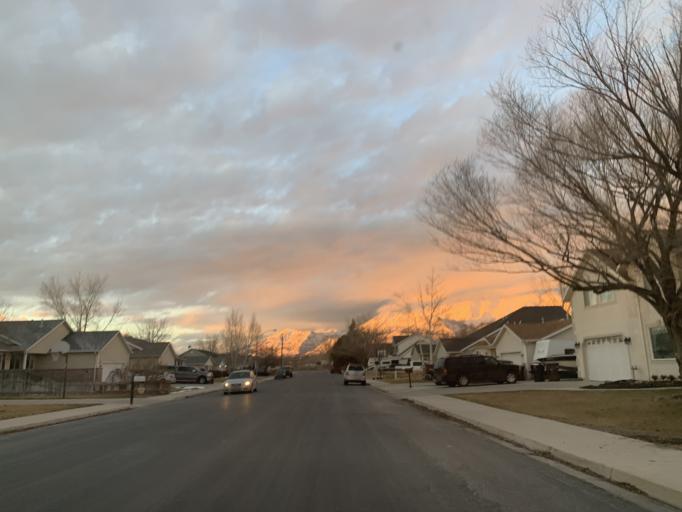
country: US
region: Utah
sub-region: Utah County
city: Provo
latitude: 40.2410
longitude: -111.7042
